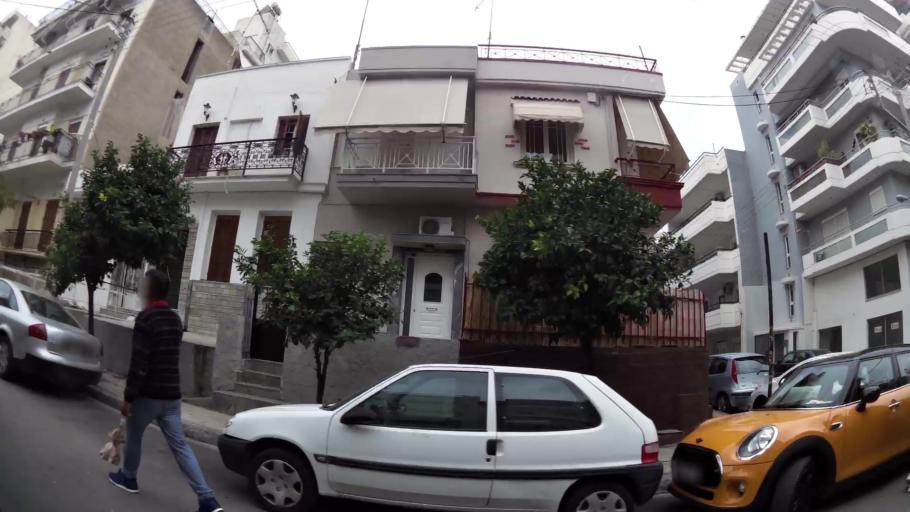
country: GR
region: Attica
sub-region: Nomos Attikis
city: Piraeus
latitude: 37.9345
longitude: 23.6332
